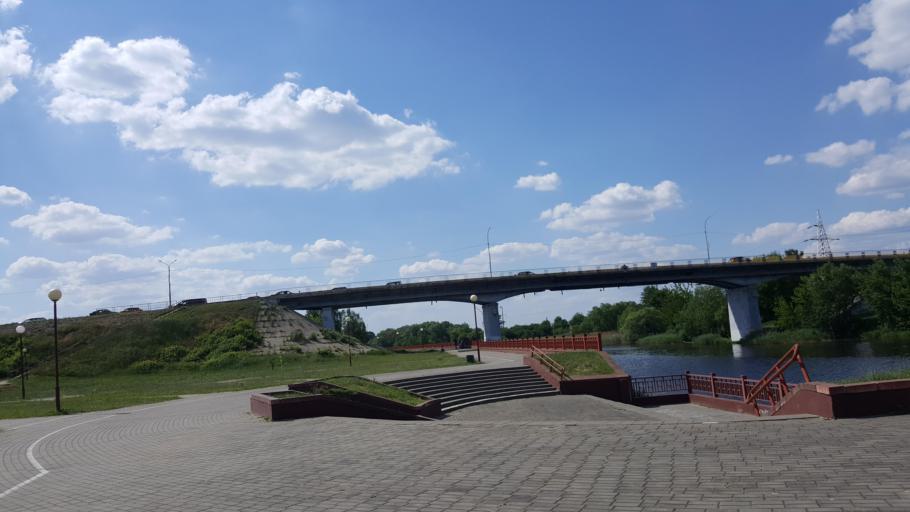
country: BY
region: Brest
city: Kobryn
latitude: 52.2149
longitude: 24.3603
